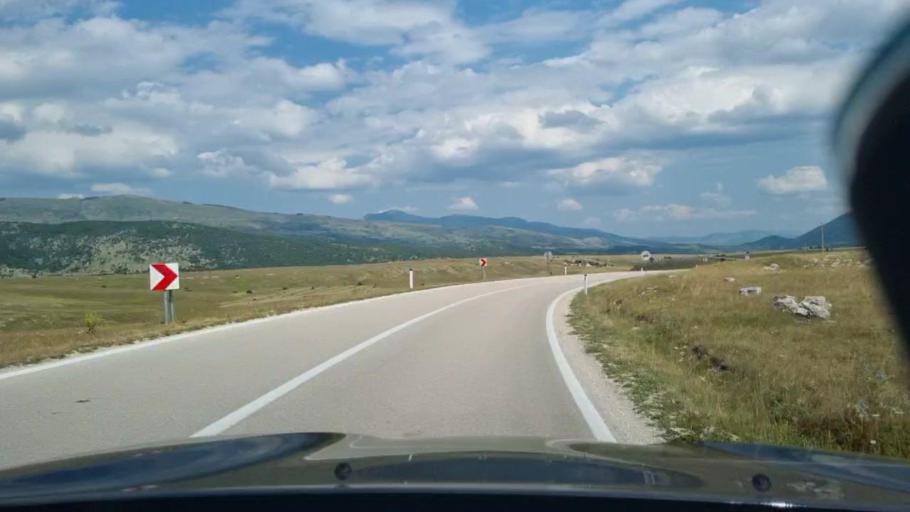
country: BA
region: Federation of Bosnia and Herzegovina
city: Bosansko Grahovo
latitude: 44.1596
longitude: 16.4227
